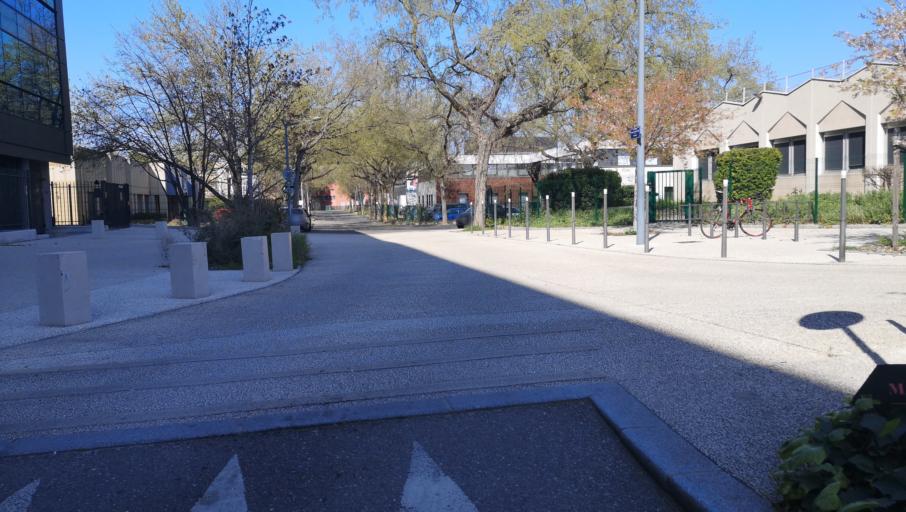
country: FR
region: Rhone-Alpes
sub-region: Departement du Rhone
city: Lyon
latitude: 45.7268
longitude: 4.8439
